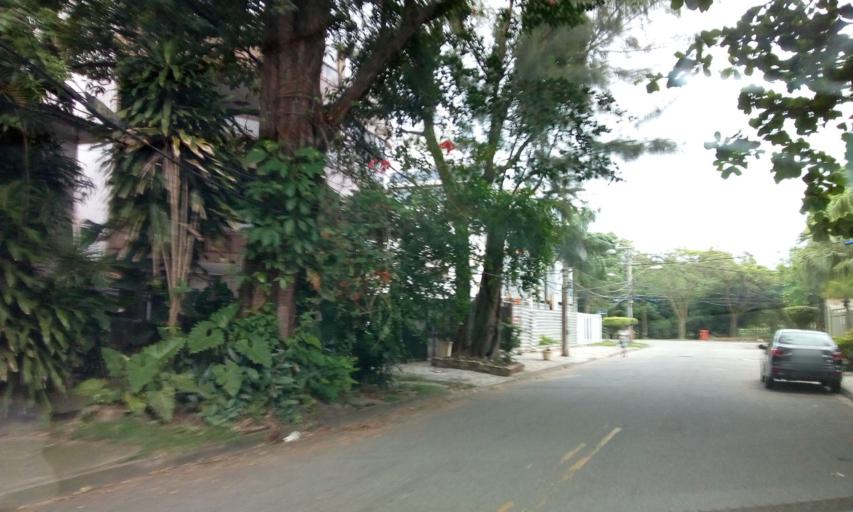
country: BR
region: Rio de Janeiro
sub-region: Nilopolis
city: Nilopolis
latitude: -23.0171
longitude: -43.4500
